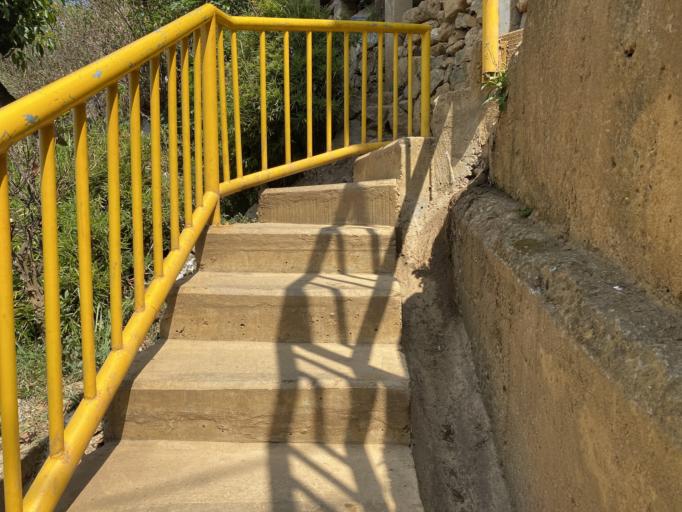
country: CO
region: Antioquia
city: Medellin
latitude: 6.2674
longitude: -75.5416
